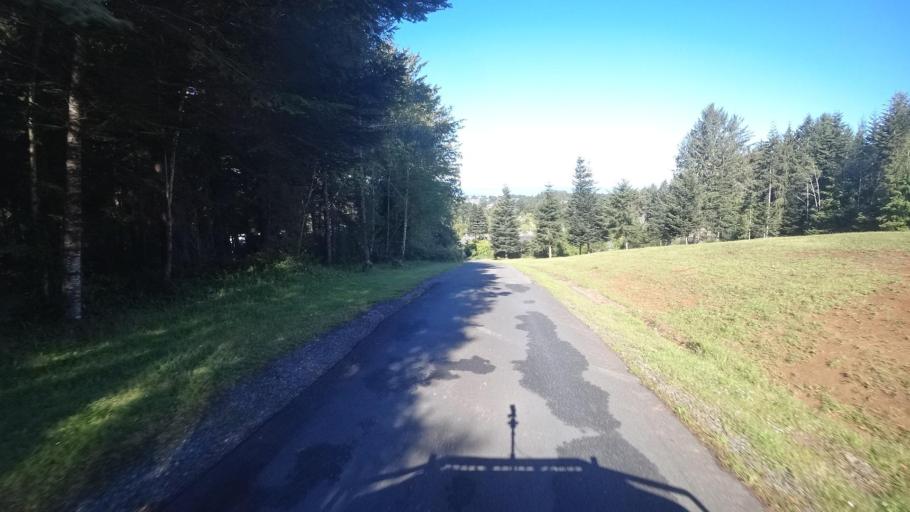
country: US
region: California
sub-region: Humboldt County
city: McKinleyville
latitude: 40.9634
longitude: -124.0902
